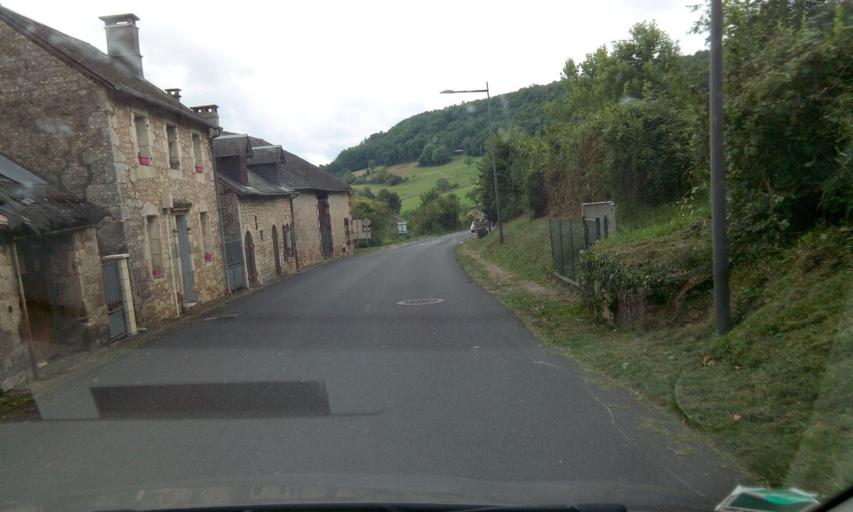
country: FR
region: Limousin
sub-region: Departement de la Correze
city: Cosnac
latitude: 45.0527
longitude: 1.5821
